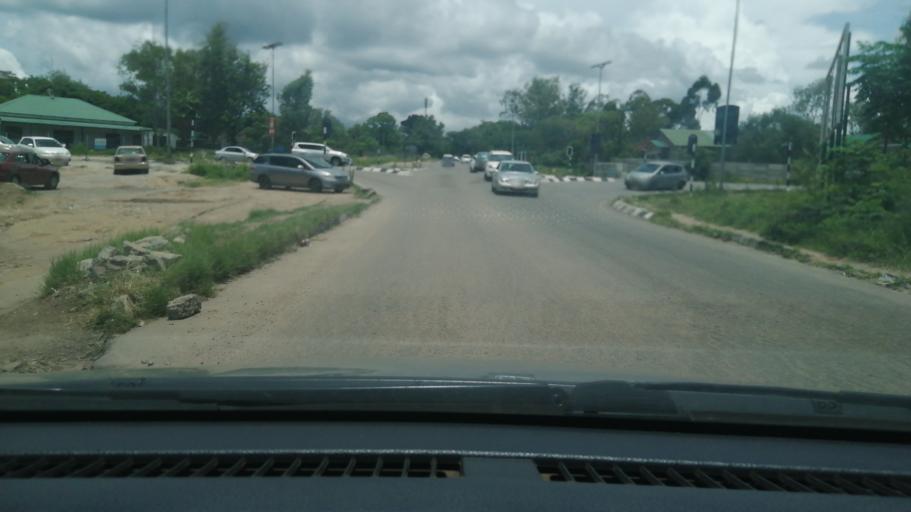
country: ZW
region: Harare
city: Harare
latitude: -17.8818
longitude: 31.0795
